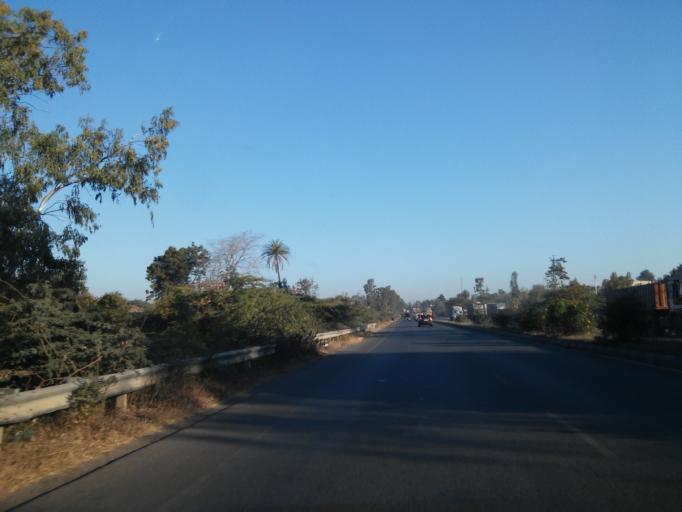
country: IN
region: Rajasthan
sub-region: Dungarpur
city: Dungarpur
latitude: 23.8249
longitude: 73.5210
